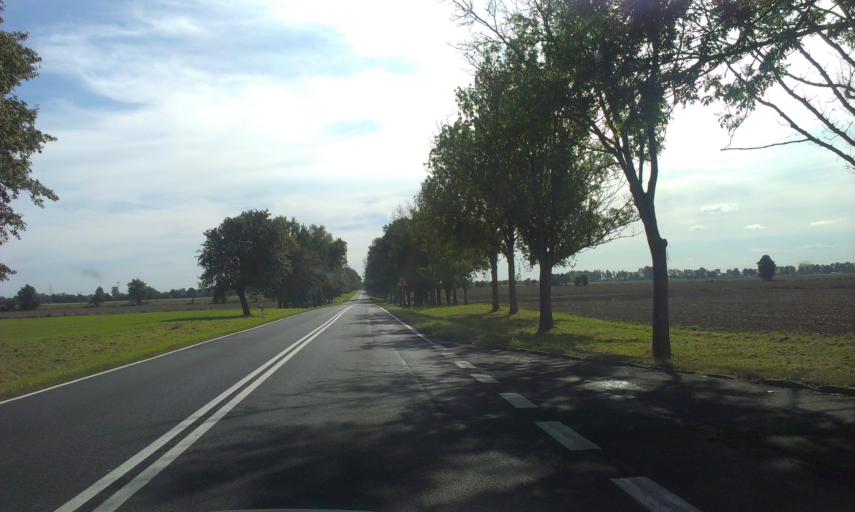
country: PL
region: Greater Poland Voivodeship
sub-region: Powiat zlotowski
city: Okonek
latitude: 53.6174
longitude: 16.7863
